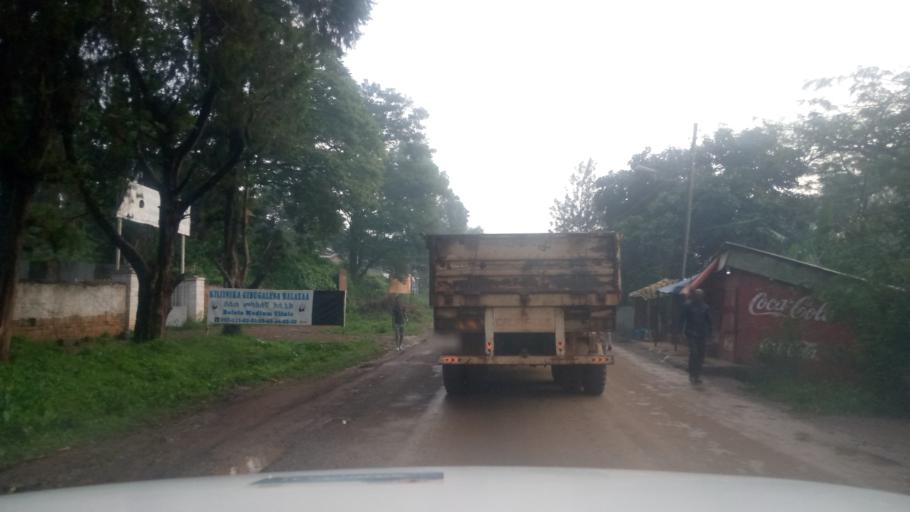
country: ET
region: Oromiya
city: Jima
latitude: 7.6781
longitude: 36.8344
